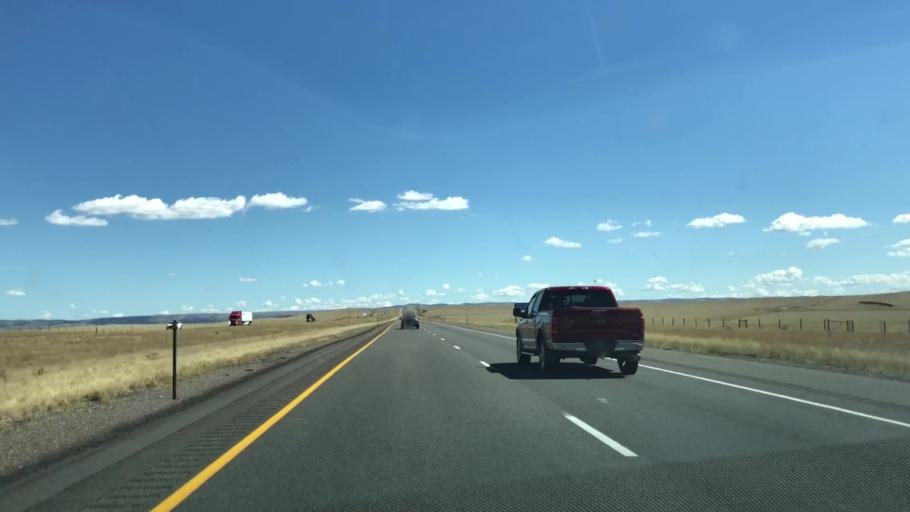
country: US
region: Wyoming
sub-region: Albany County
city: Laramie
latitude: 41.3540
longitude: -105.7395
